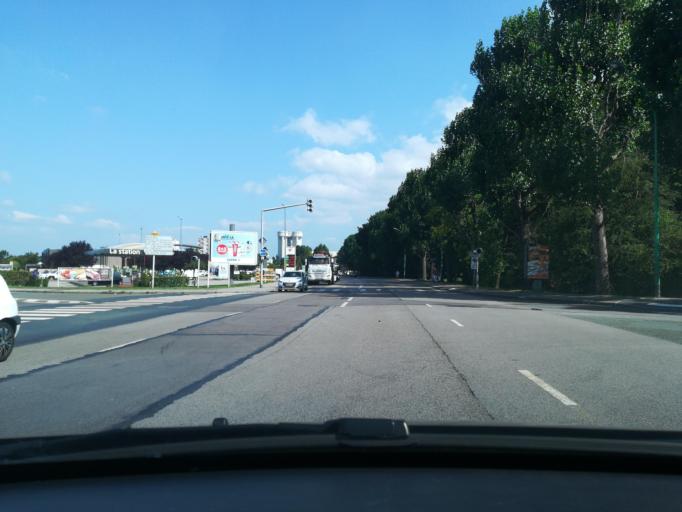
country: FR
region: Haute-Normandie
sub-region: Departement de la Seine-Maritime
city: Bois-Guillaume
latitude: 49.4621
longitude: 1.1224
